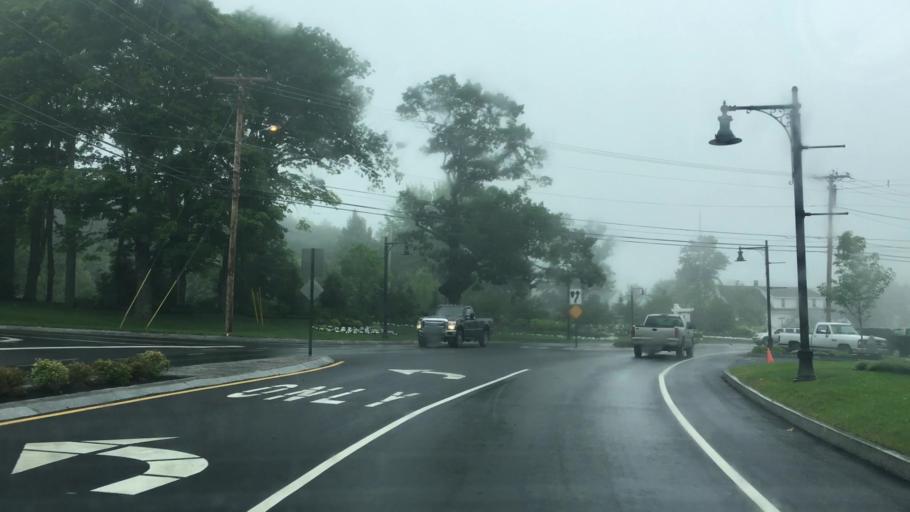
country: US
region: Maine
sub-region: Lincoln County
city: Boothbay
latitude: 43.8776
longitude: -69.6325
